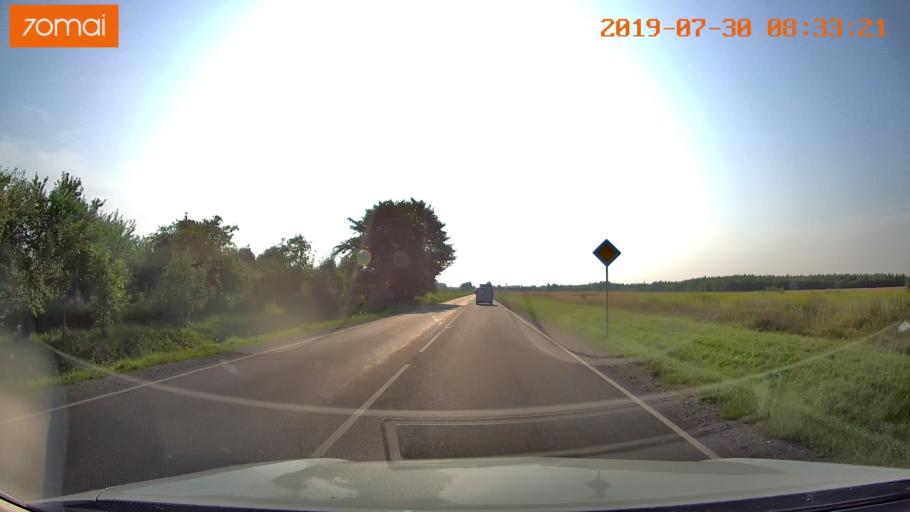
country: RU
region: Kaliningrad
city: Chernyakhovsk
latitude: 54.6359
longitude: 21.7460
